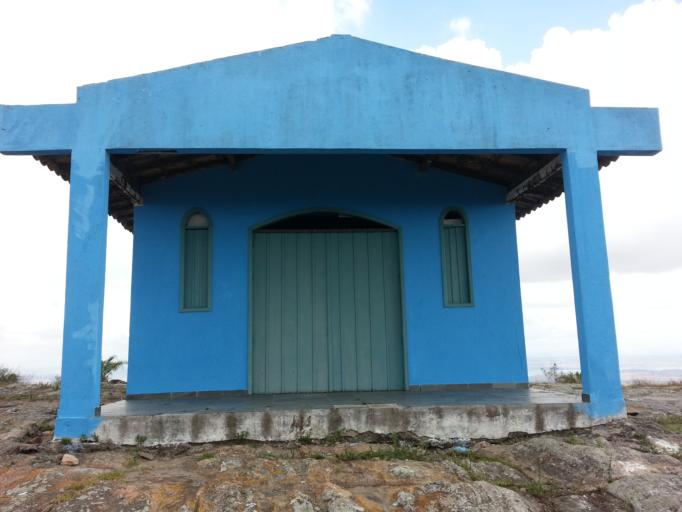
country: BR
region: Bahia
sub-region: Cruz Das Almas
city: Cruz das Almas
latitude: -12.6002
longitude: -39.1902
